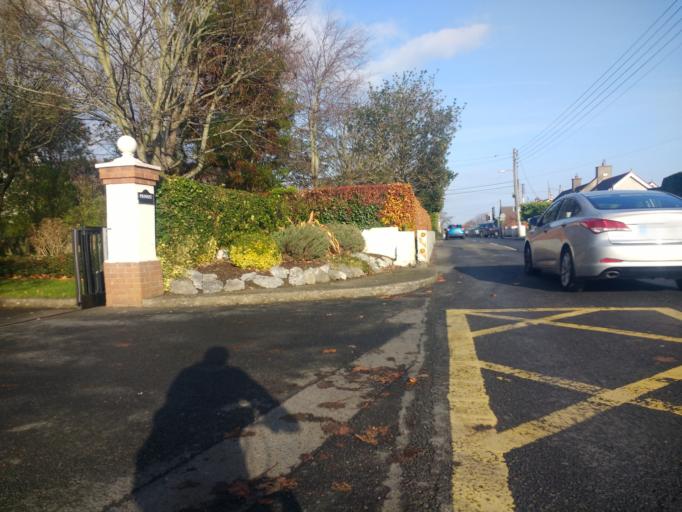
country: IE
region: Leinster
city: Malahide
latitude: 53.4518
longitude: -6.1734
